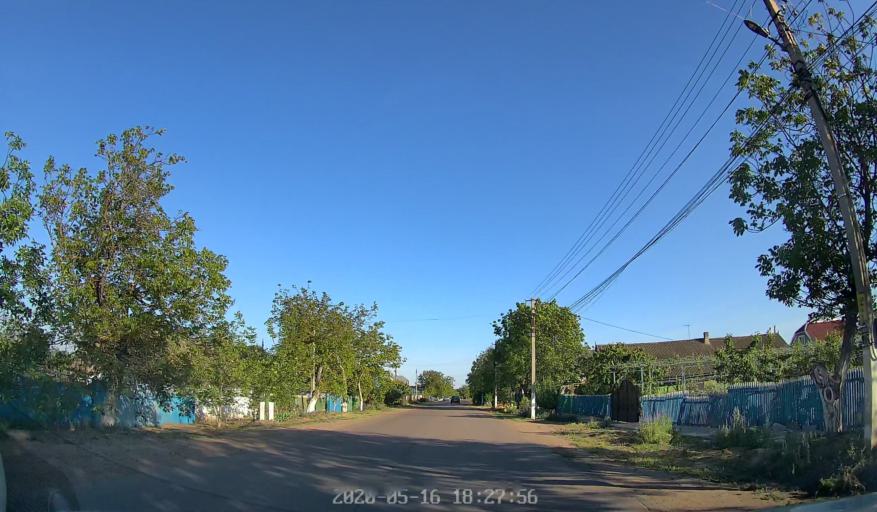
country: MD
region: Telenesti
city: Dnestrovsc
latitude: 46.5440
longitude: 30.0123
